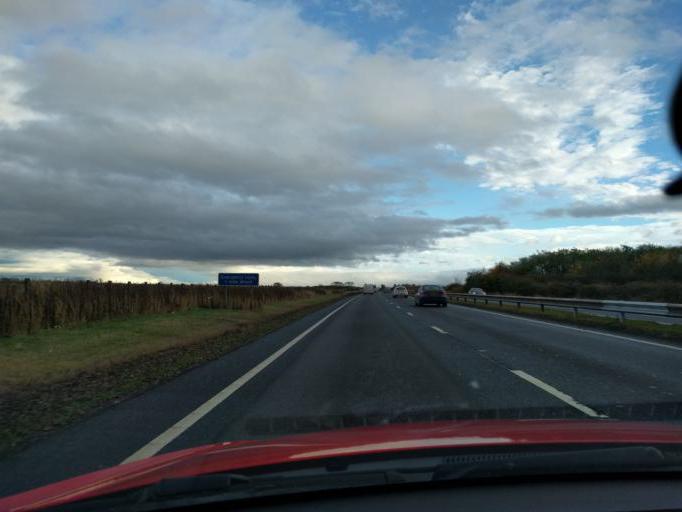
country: GB
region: Scotland
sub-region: East Lothian
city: Macmerry
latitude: 55.9505
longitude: -2.9255
